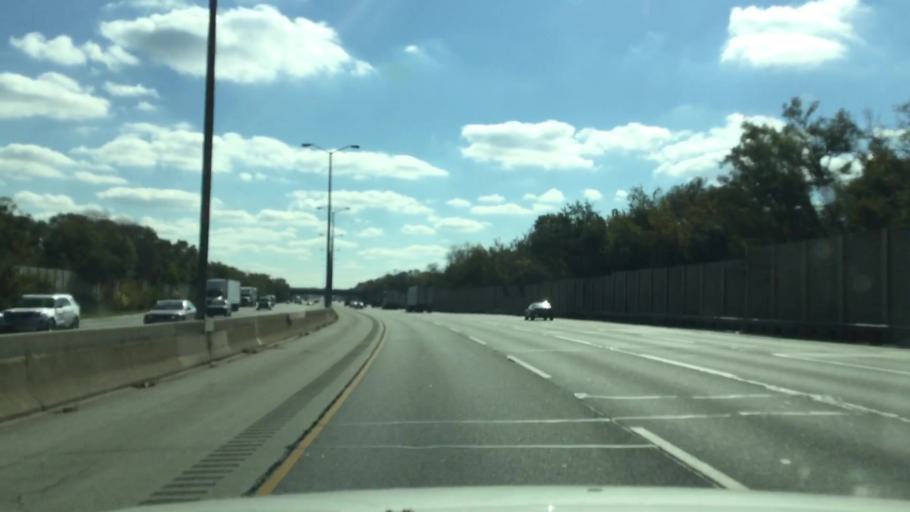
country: US
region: Illinois
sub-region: Cook County
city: Western Springs
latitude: 41.8114
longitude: -87.9137
